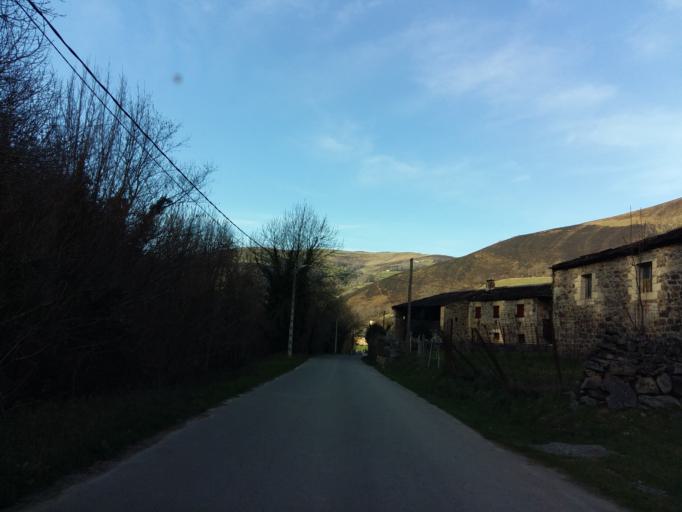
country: ES
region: Cantabria
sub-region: Provincia de Cantabria
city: Vega de Pas
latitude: 43.1491
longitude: -3.8022
